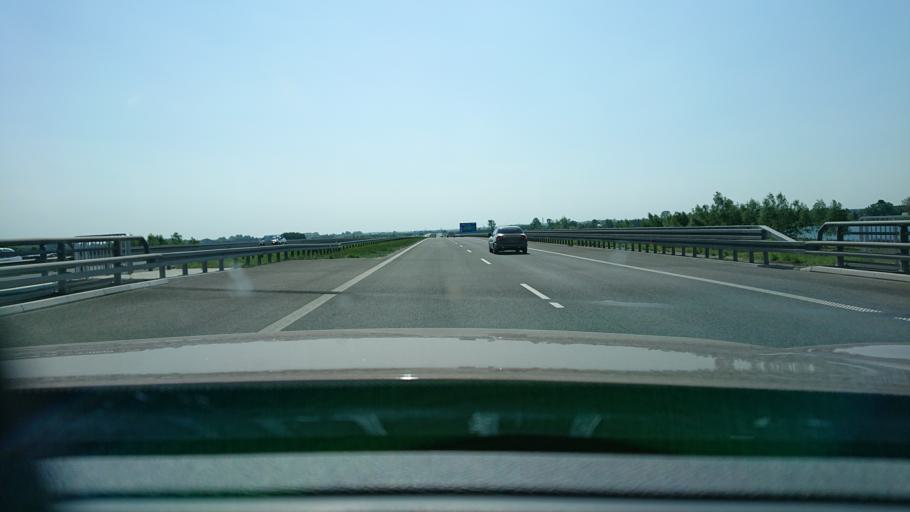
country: PL
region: Subcarpathian Voivodeship
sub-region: Powiat przeworski
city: Grzeska
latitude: 50.1005
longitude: 22.4540
